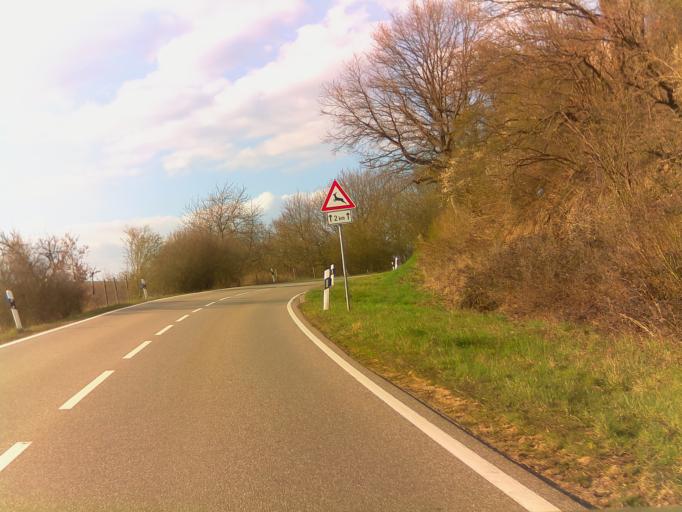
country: DE
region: Rheinland-Pfalz
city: Meisenheim
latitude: 49.7158
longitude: 7.6702
